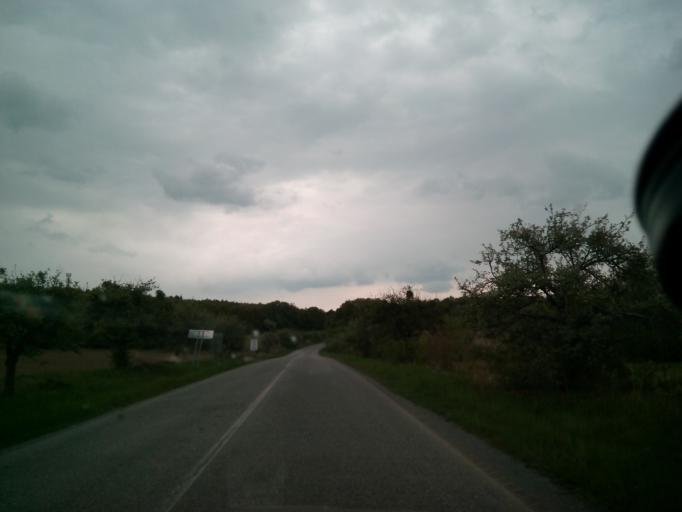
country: SK
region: Kosicky
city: Secovce
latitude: 48.7983
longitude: 21.4814
